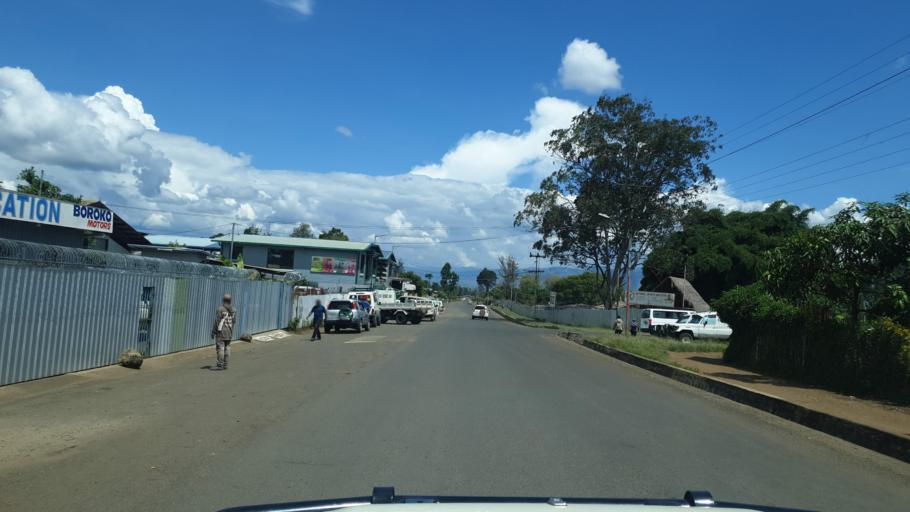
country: PG
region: Eastern Highlands
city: Goroka
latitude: -6.0832
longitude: 145.3878
